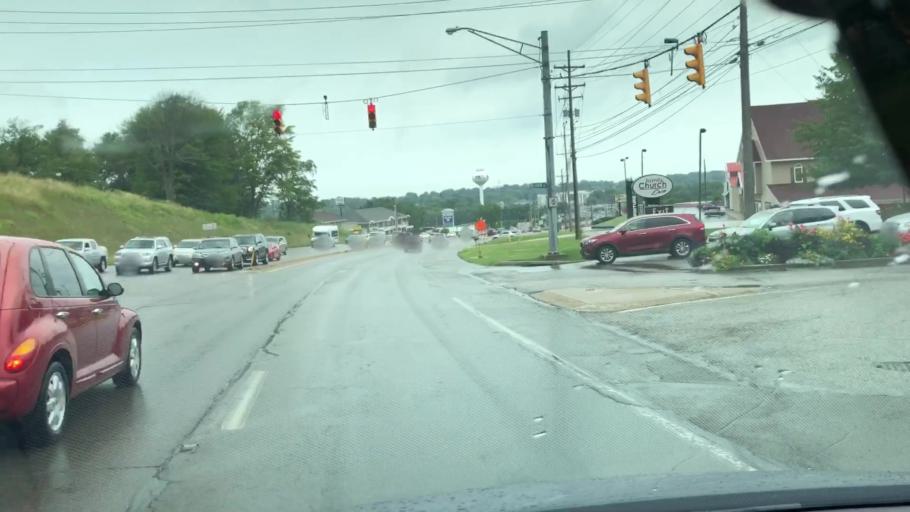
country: US
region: Pennsylvania
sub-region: Erie County
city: Erie
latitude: 42.0612
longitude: -80.0937
